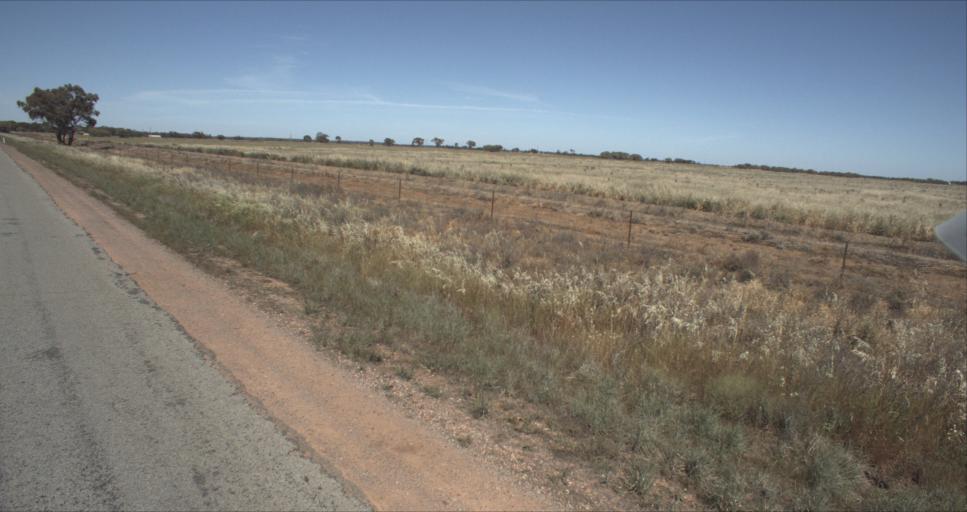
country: AU
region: New South Wales
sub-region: Leeton
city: Leeton
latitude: -34.5618
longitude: 146.3126
